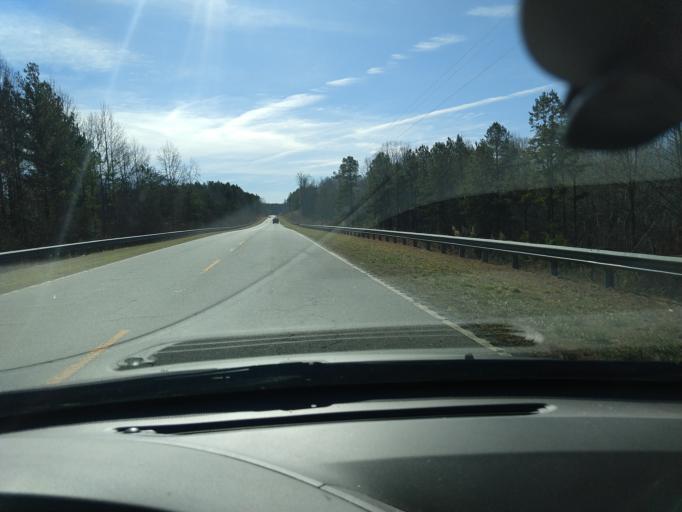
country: US
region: South Carolina
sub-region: Oconee County
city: Westminster
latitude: 34.6340
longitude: -83.1354
